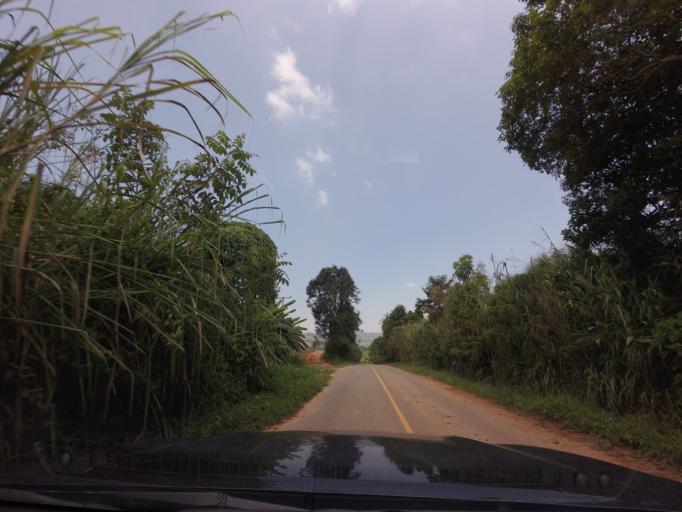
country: TH
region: Loei
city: Na Haeo
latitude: 17.5288
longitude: 100.8796
